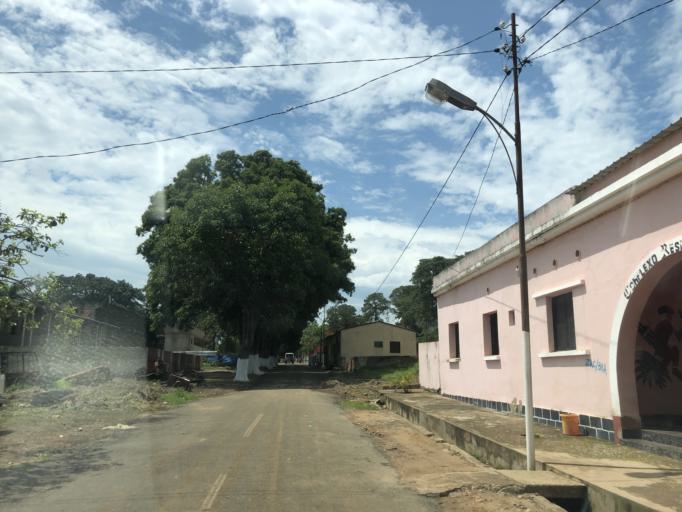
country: AO
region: Cuanza Sul
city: Quibala
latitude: -10.7337
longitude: 14.9791
